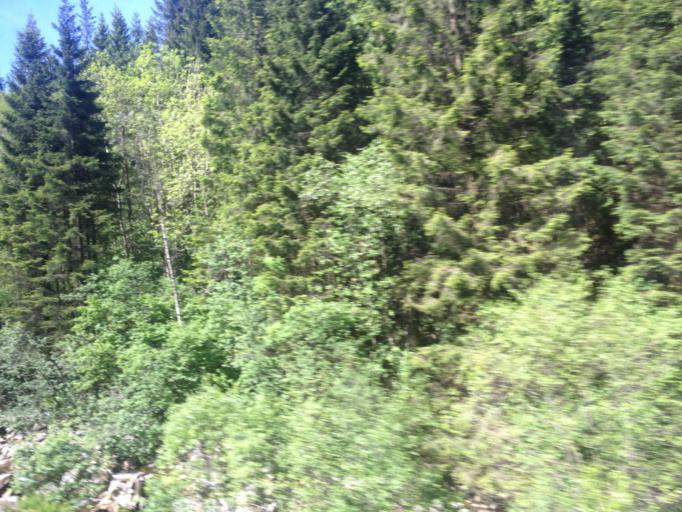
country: NO
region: Rogaland
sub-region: Lund
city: Moi
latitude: 58.4736
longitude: 6.4155
